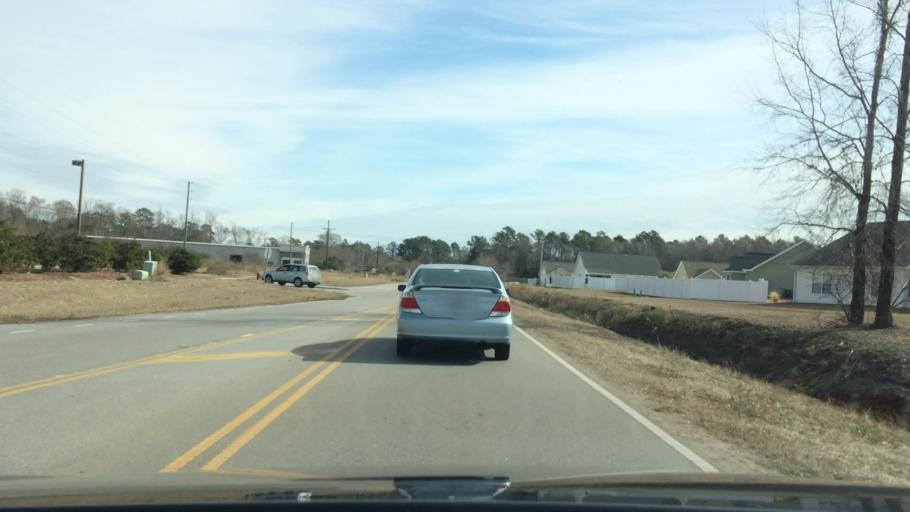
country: US
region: South Carolina
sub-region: Horry County
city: Socastee
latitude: 33.6774
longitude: -78.9753
